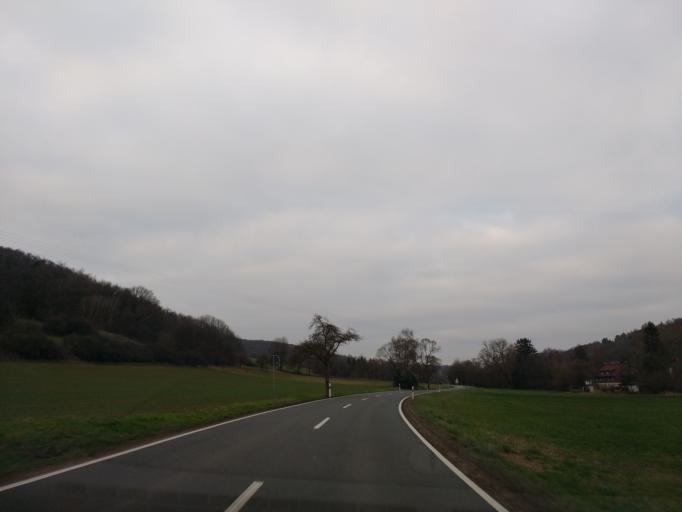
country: DE
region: Hesse
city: Bebra
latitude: 50.9982
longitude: 9.7665
